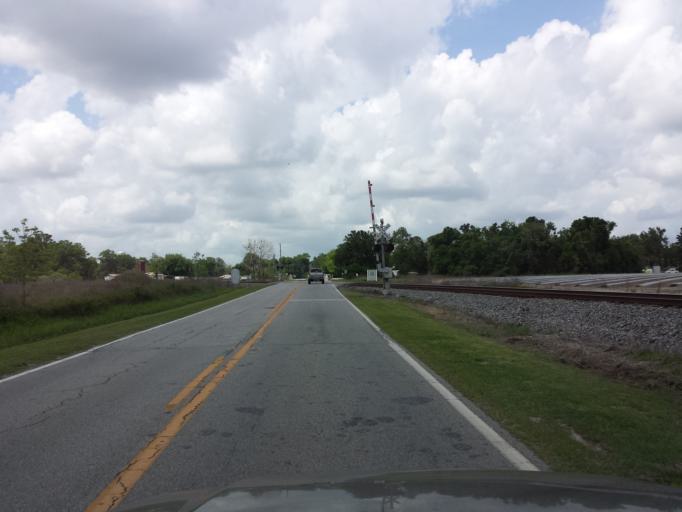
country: US
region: Georgia
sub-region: Echols County
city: Statenville
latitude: 30.6804
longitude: -83.1752
